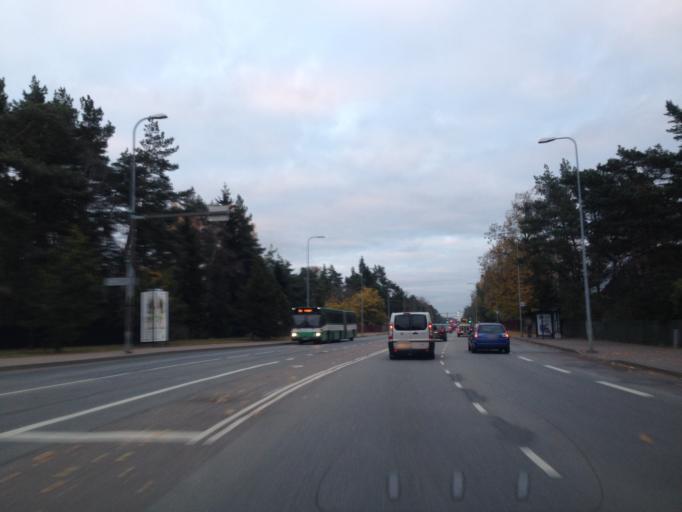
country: EE
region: Harju
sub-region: Saue vald
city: Laagri
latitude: 59.3735
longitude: 24.6661
